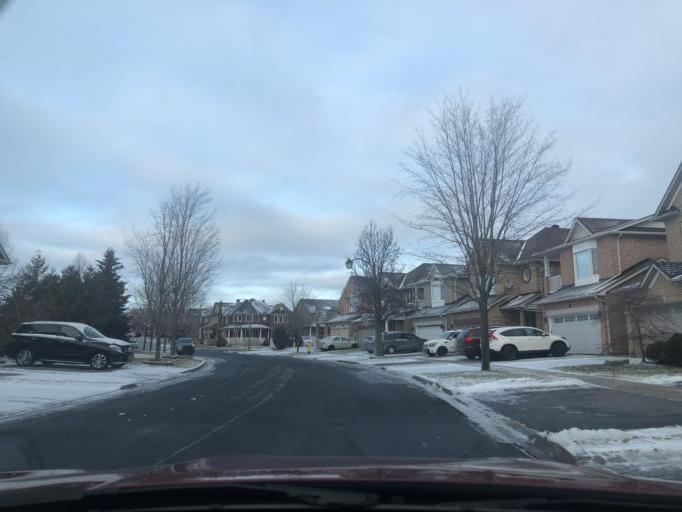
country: CA
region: Ontario
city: Markham
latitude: 43.8650
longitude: -79.2363
